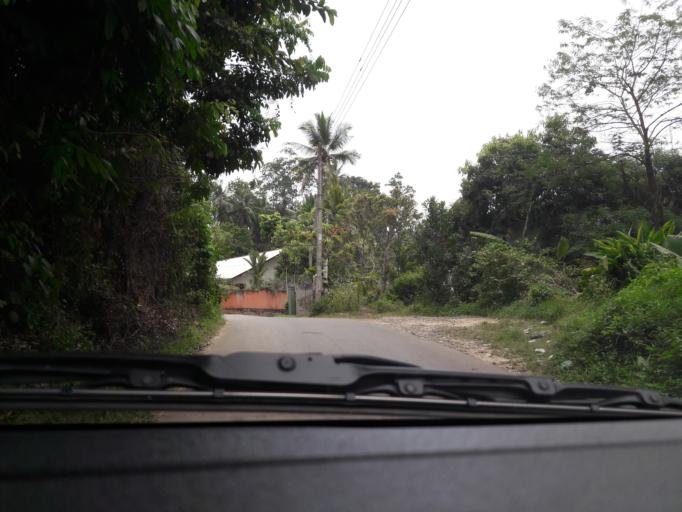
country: LK
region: Southern
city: Unawatuna
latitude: 6.0508
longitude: 80.2489
